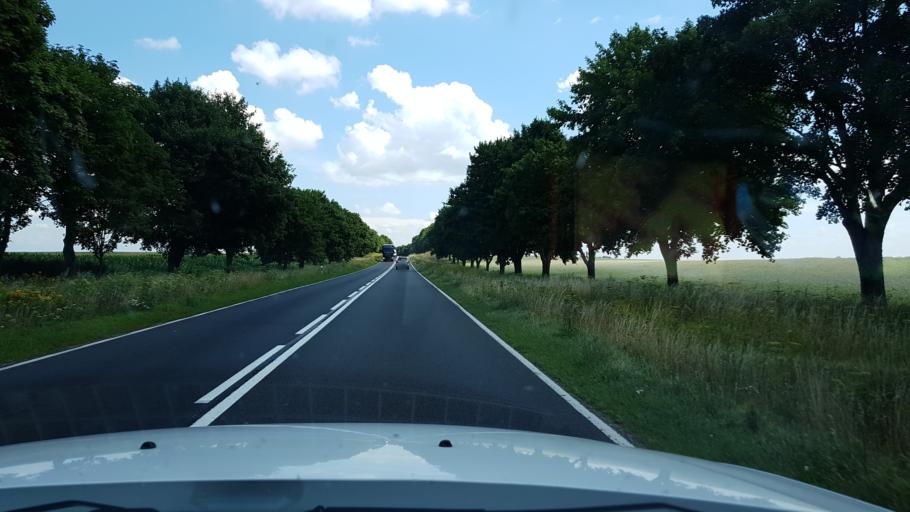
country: PL
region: West Pomeranian Voivodeship
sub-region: Powiat stargardzki
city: Dobrzany
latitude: 53.2730
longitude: 15.4223
